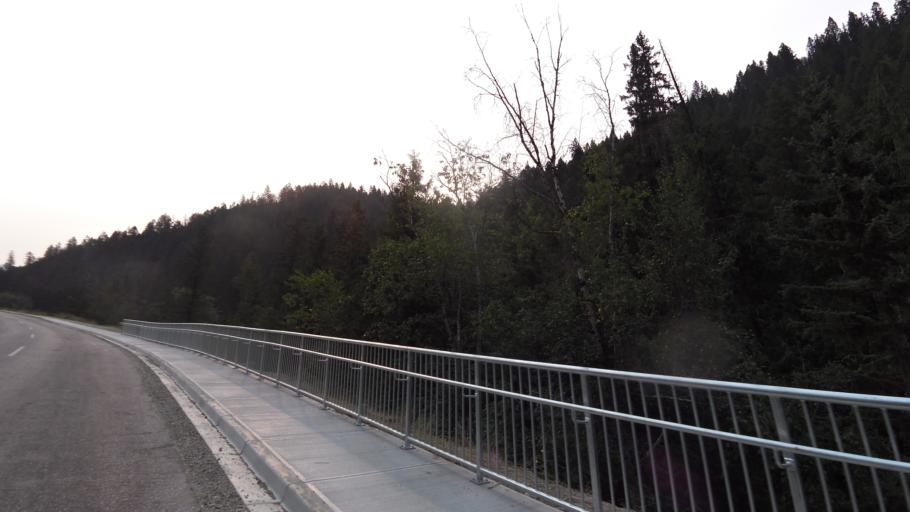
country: CA
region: British Columbia
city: Invermere
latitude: 50.6334
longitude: -116.0464
